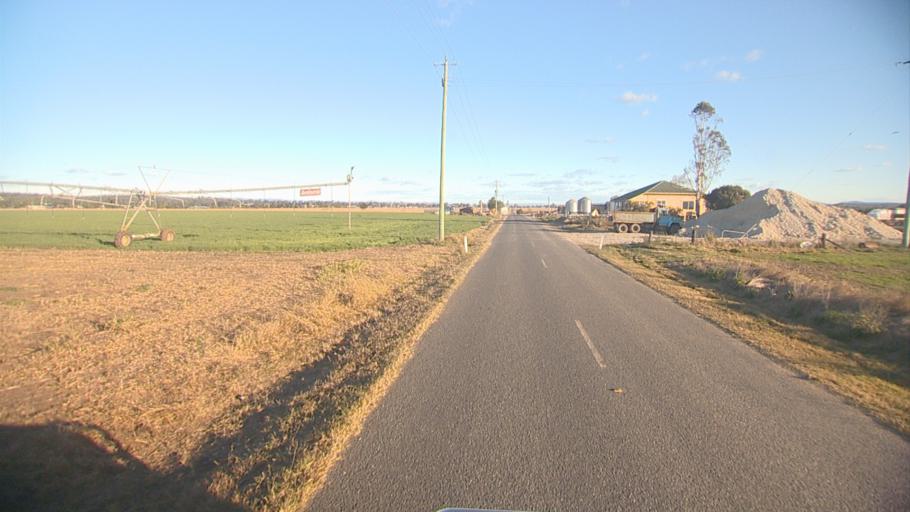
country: AU
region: Queensland
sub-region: Logan
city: Cedar Vale
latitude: -27.8566
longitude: 152.9598
